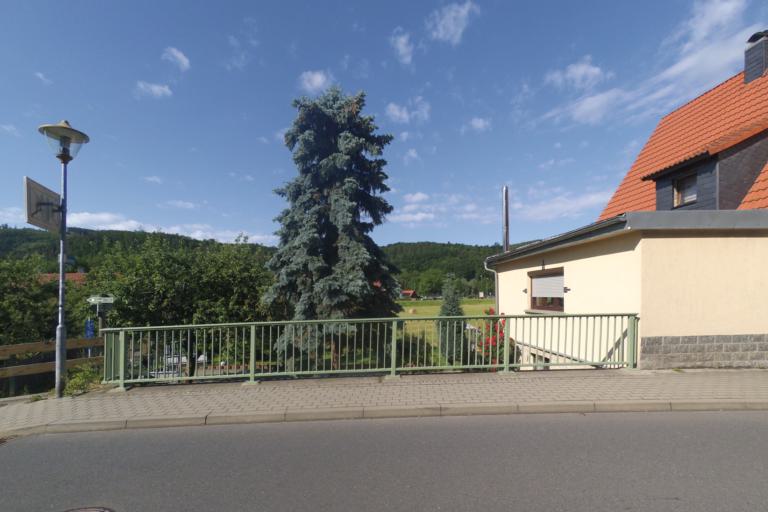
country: DE
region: Thuringia
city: Kaulsdorf
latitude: 50.6163
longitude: 11.4316
